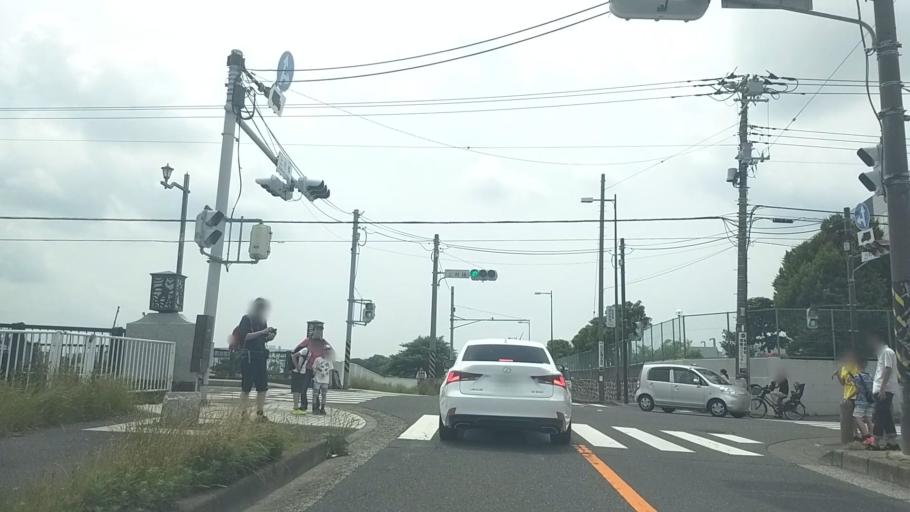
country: JP
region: Kanagawa
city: Fujisawa
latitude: 35.3423
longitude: 139.4666
